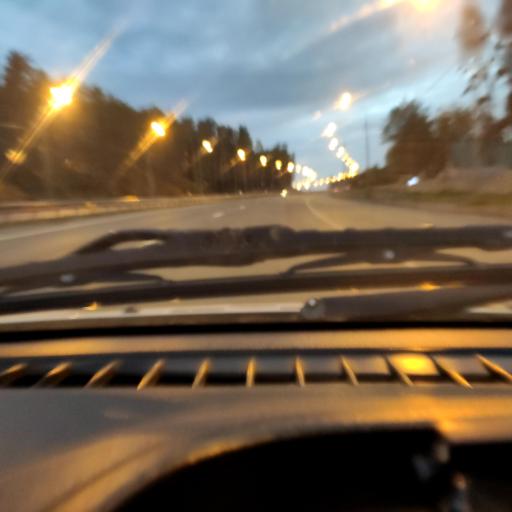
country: RU
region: Samara
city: Zhigulevsk
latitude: 53.5346
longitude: 49.5164
